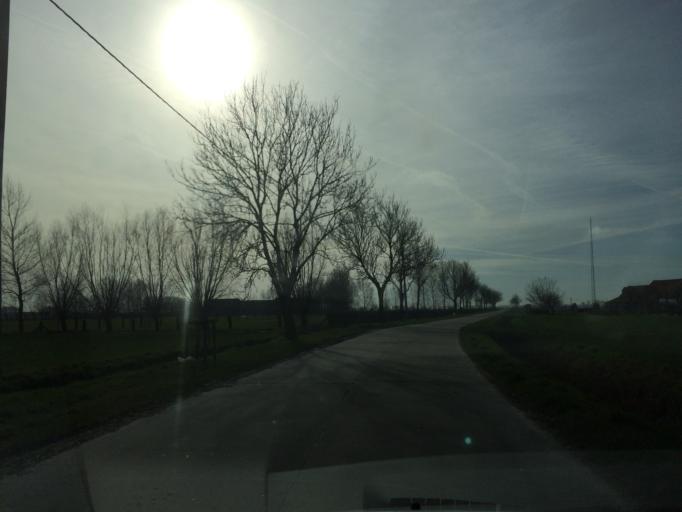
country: BE
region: Flanders
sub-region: Provincie West-Vlaanderen
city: Nieuwpoort
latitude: 51.1078
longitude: 2.7981
